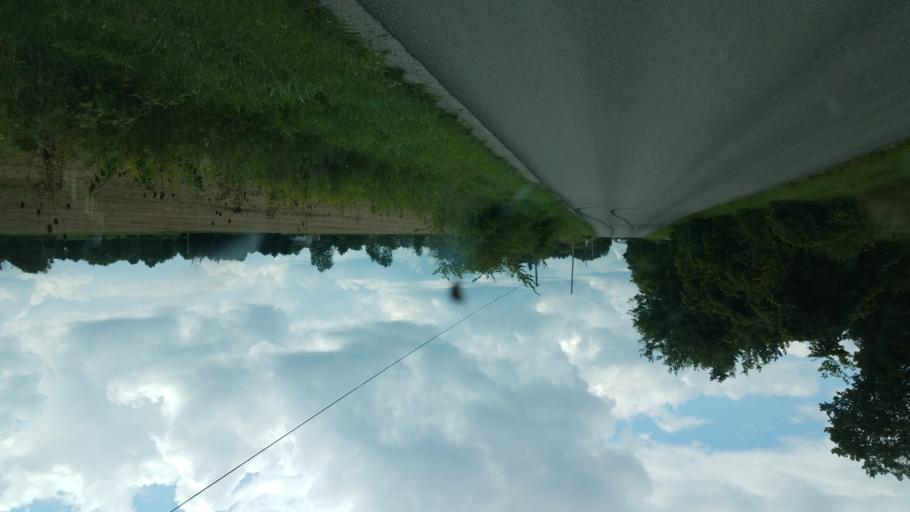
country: US
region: Ohio
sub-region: Knox County
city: Centerburg
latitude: 40.3930
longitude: -82.8003
